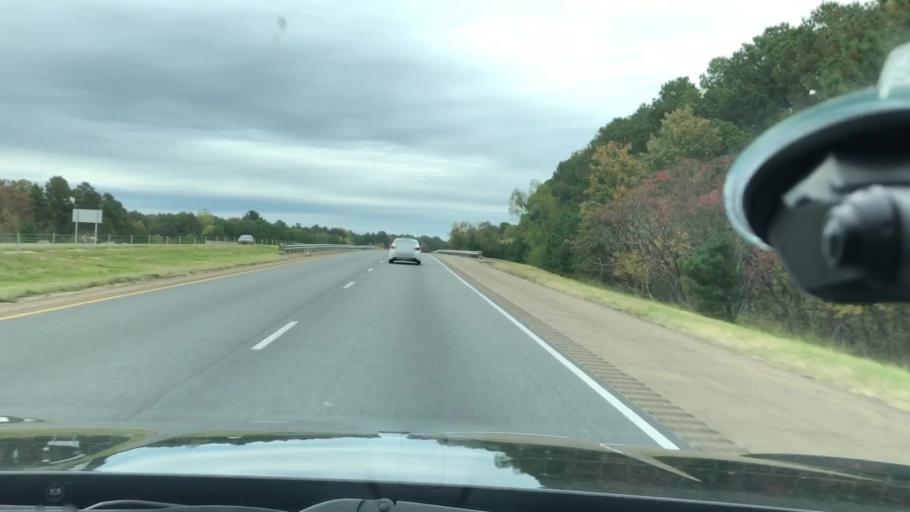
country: US
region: Arkansas
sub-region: Clark County
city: Gurdon
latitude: 33.9497
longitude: -93.2346
